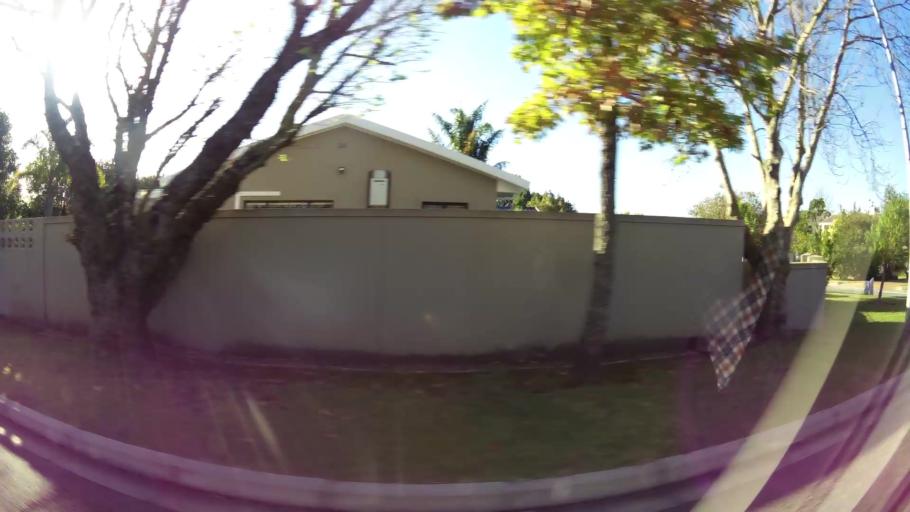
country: ZA
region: Western Cape
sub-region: Eden District Municipality
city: George
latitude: -33.9437
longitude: 22.4568
